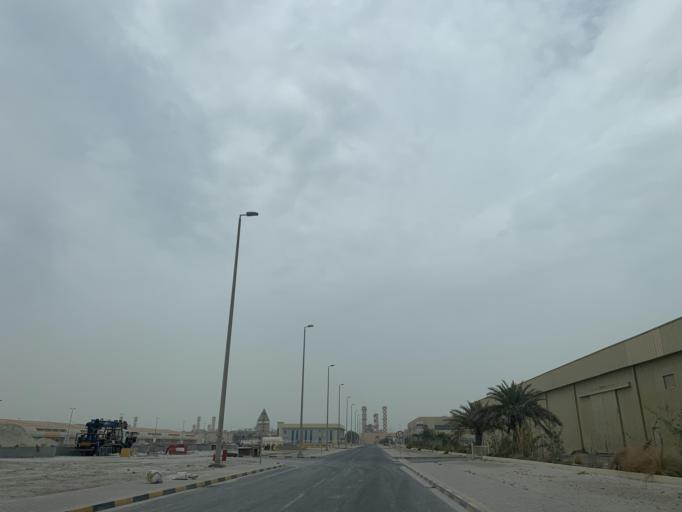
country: BH
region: Muharraq
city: Al Hadd
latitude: 26.2222
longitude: 50.6727
